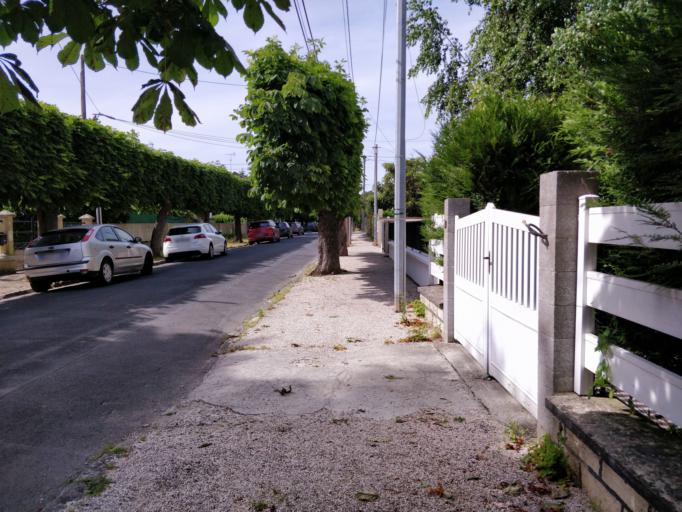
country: FR
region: Ile-de-France
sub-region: Departement de Seine-Saint-Denis
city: Noisy-le-Grand
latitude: 48.8618
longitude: 2.5696
